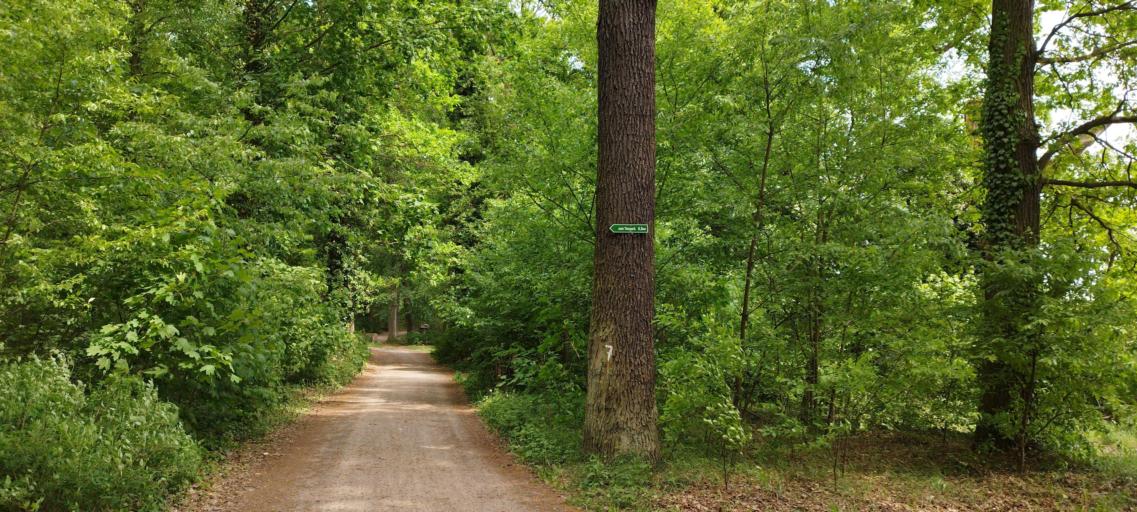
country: DE
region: Brandenburg
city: Furstenwalde
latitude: 52.3646
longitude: 14.0471
